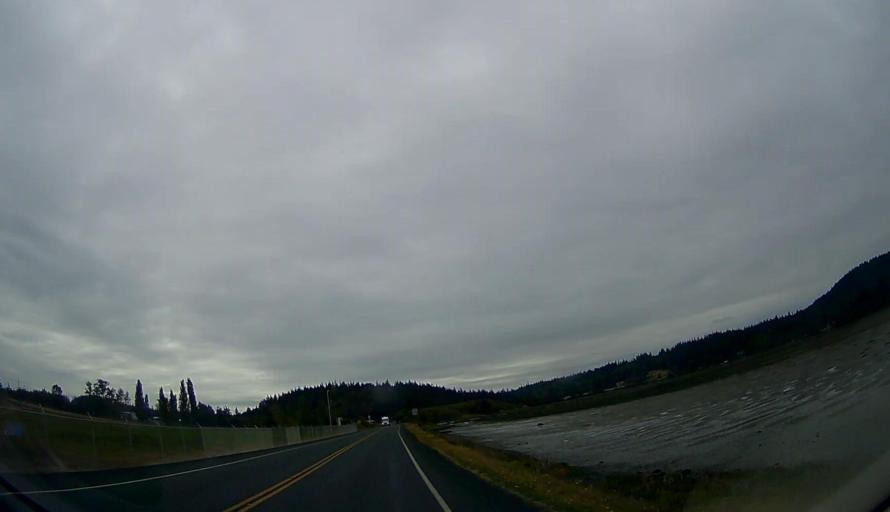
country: US
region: Washington
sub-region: Skagit County
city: Anacortes
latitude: 48.4676
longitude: -122.5708
